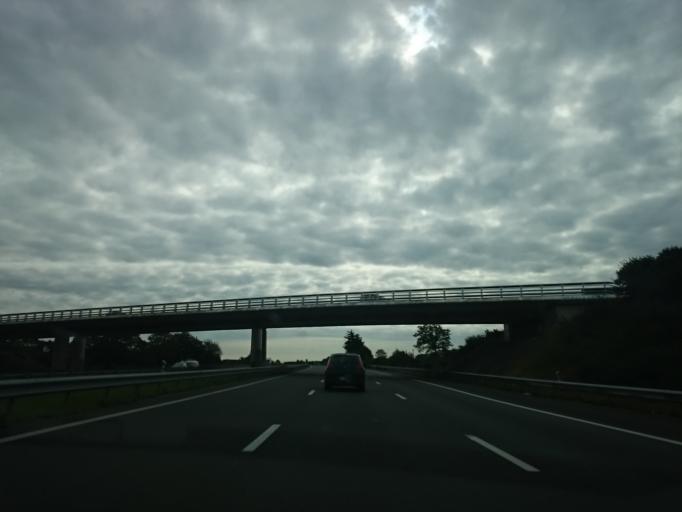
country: FR
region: Pays de la Loire
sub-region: Departement de la Loire-Atlantique
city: Malville
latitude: 47.3563
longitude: -1.8924
